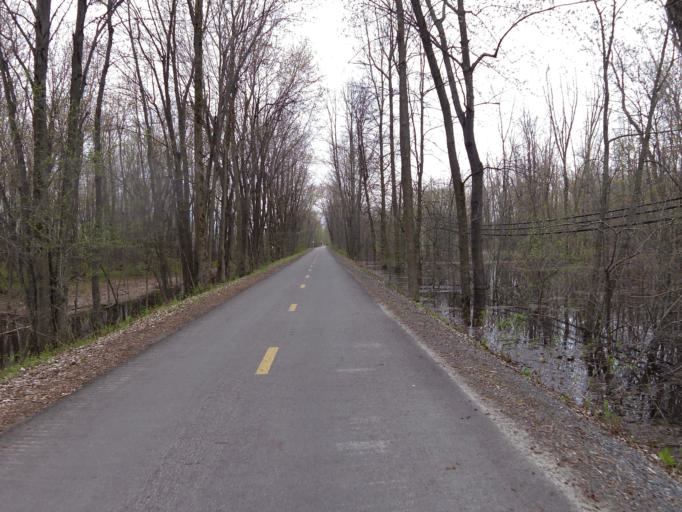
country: CA
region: Quebec
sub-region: Laurentides
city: Sainte-Marthe-sur-le-Lac
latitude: 45.5091
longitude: -73.9688
